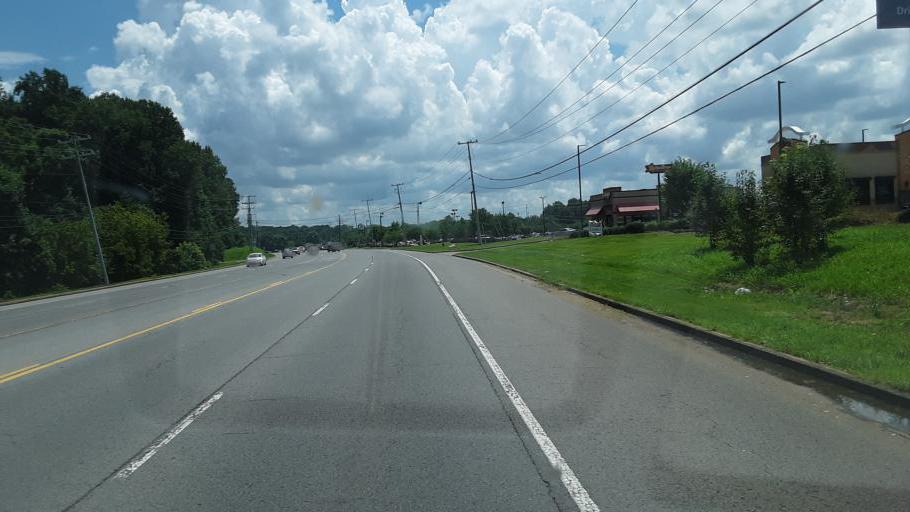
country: US
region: Kentucky
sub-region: Christian County
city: Oak Grove
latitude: 36.6276
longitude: -87.3740
